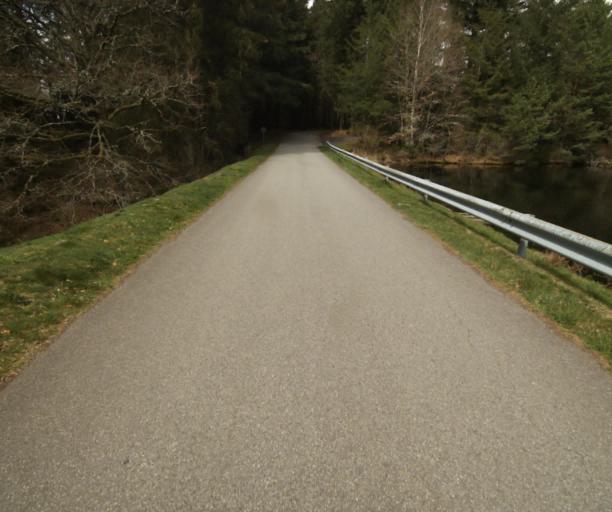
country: FR
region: Limousin
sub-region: Departement de la Correze
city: Correze
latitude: 45.3393
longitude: 1.9498
